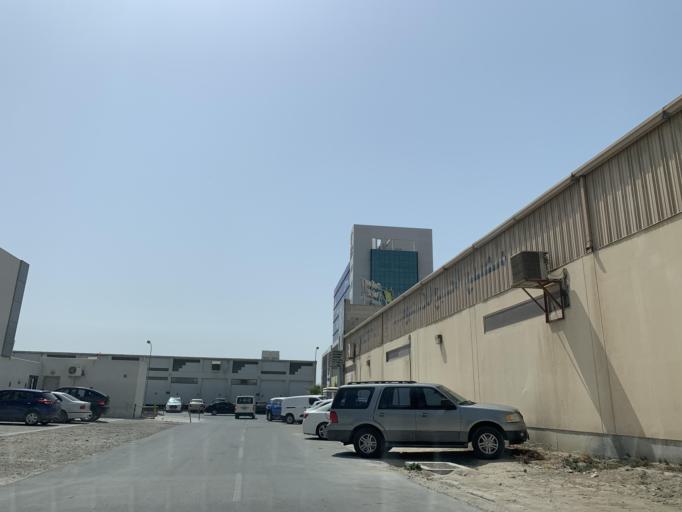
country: BH
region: Northern
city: Madinat `Isa
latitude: 26.1901
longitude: 50.5379
